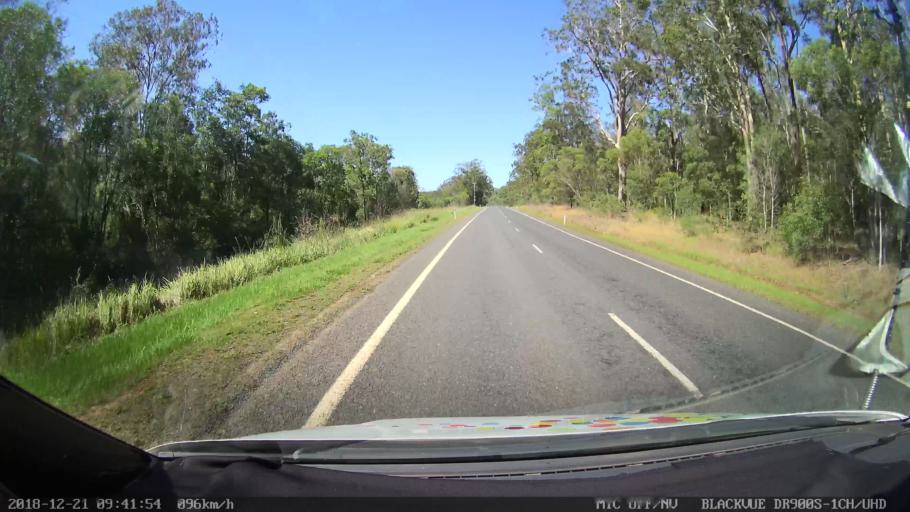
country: AU
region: New South Wales
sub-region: Clarence Valley
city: Grafton
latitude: -29.5902
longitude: 152.9526
